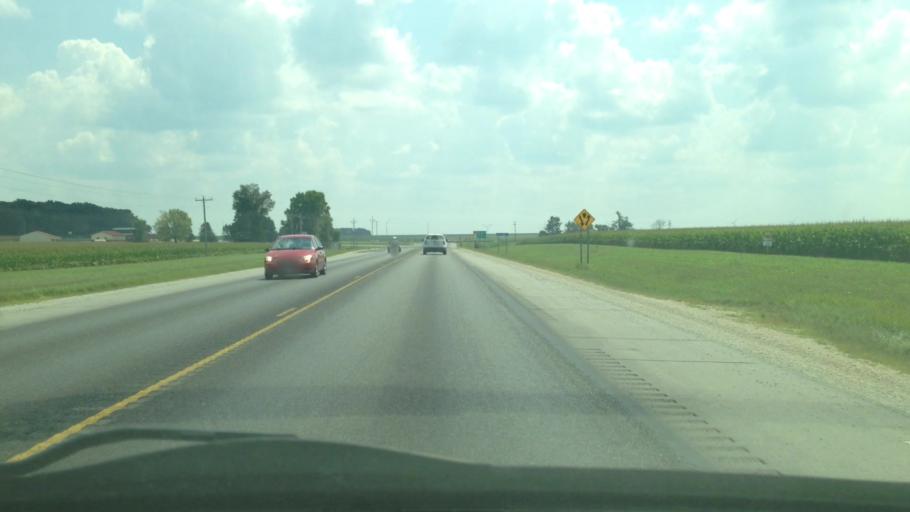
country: US
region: Minnesota
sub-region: Mower County
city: Grand Meadow
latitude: 43.7156
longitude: -92.4795
